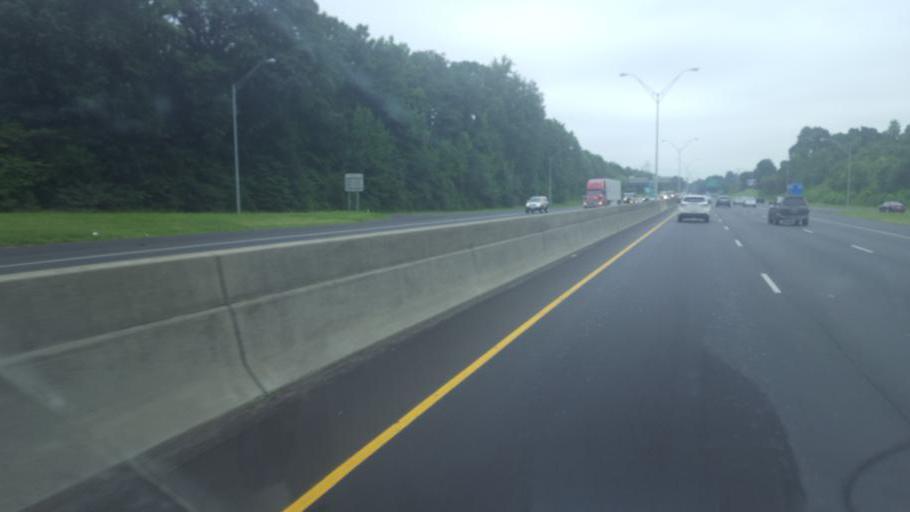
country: US
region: North Carolina
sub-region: Mecklenburg County
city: Charlotte
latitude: 35.1645
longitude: -80.8894
